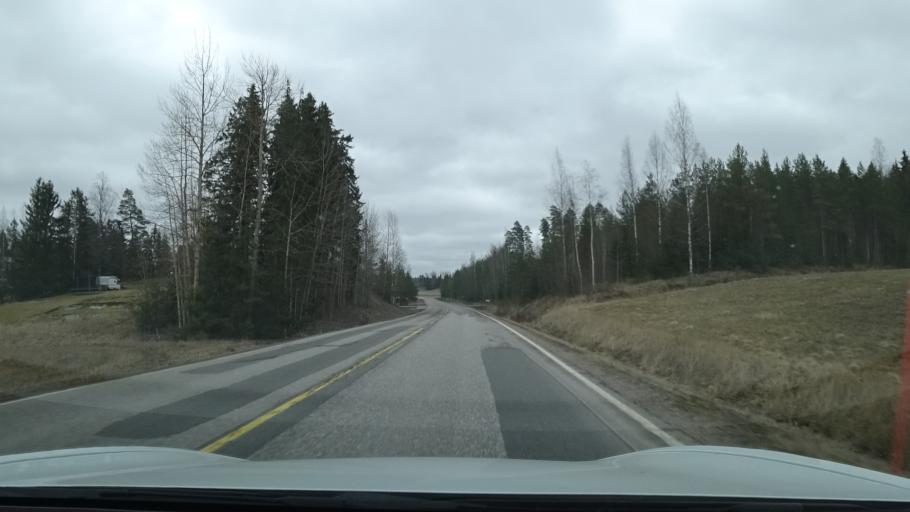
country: FI
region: Uusimaa
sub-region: Porvoo
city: Myrskylae
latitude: 60.6590
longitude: 25.8266
